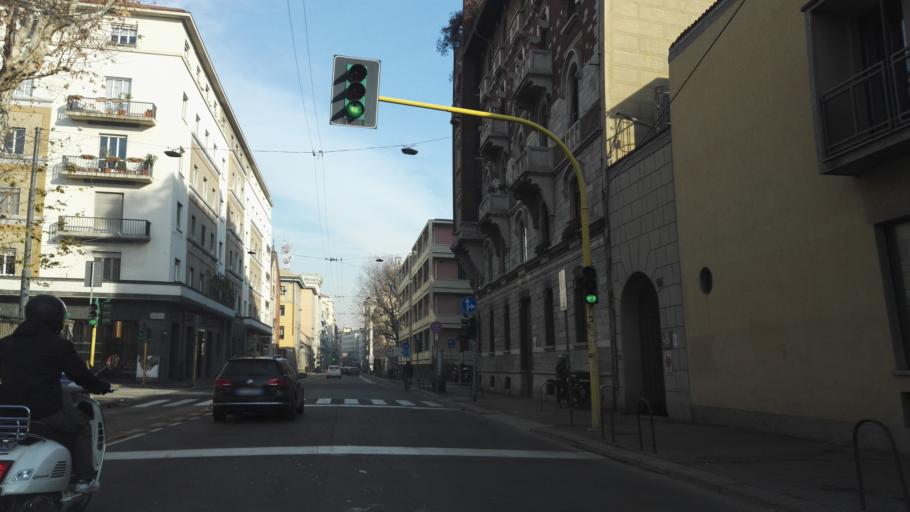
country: IT
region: Lombardy
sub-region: Citta metropolitana di Milano
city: Milano
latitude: 45.4605
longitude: 9.1963
